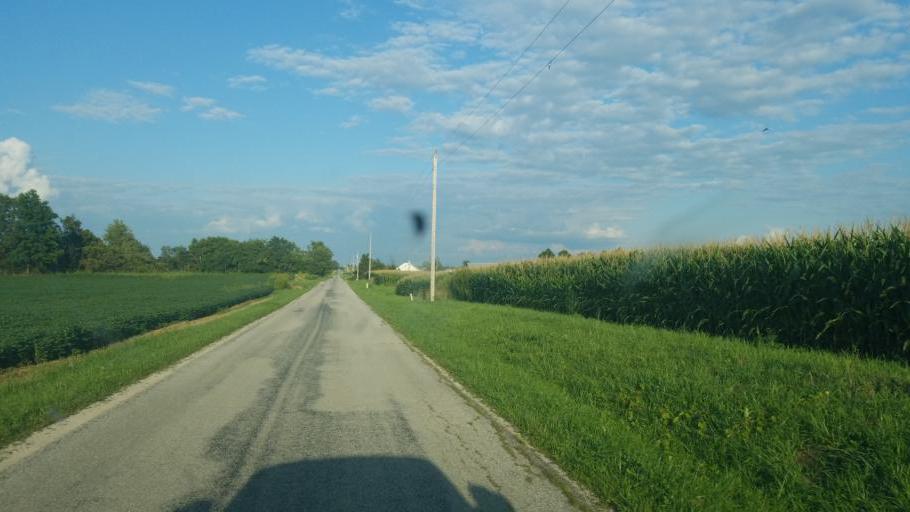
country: US
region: Ohio
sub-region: Huron County
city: Willard
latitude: 41.1098
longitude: -82.8554
